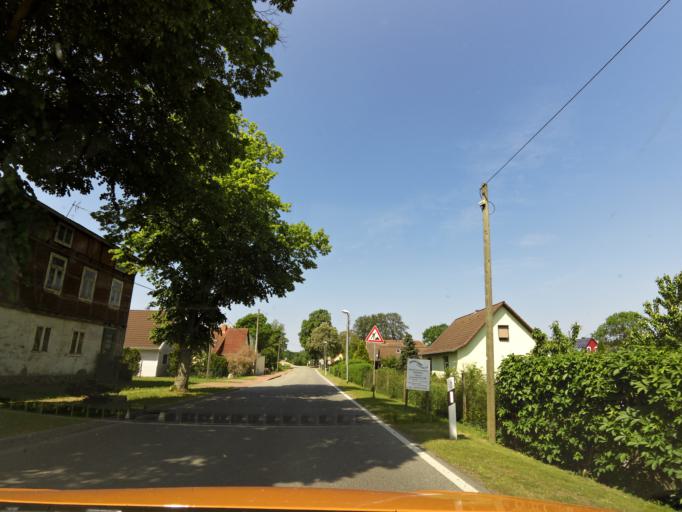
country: DE
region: Mecklenburg-Vorpommern
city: Neuburg
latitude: 53.4066
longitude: 11.9180
